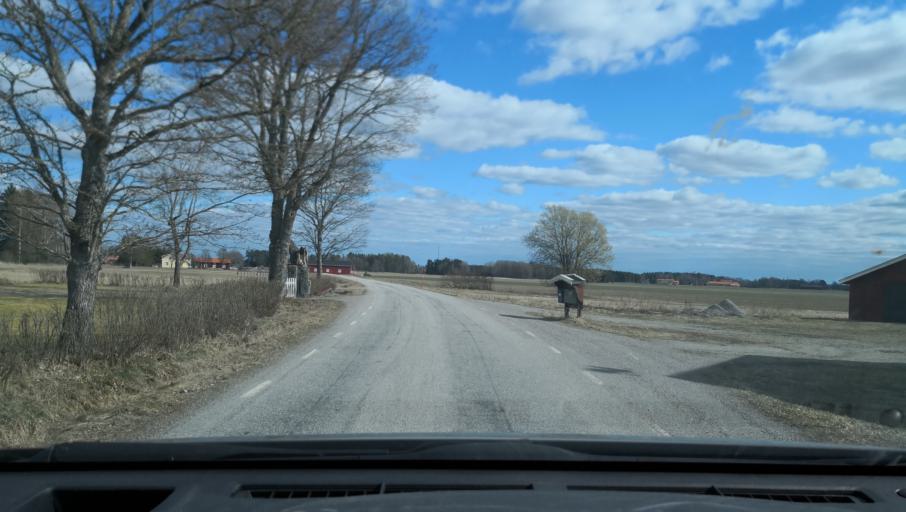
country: SE
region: Vaestmanland
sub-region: Sala Kommun
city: Sala
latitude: 59.8589
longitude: 16.6054
